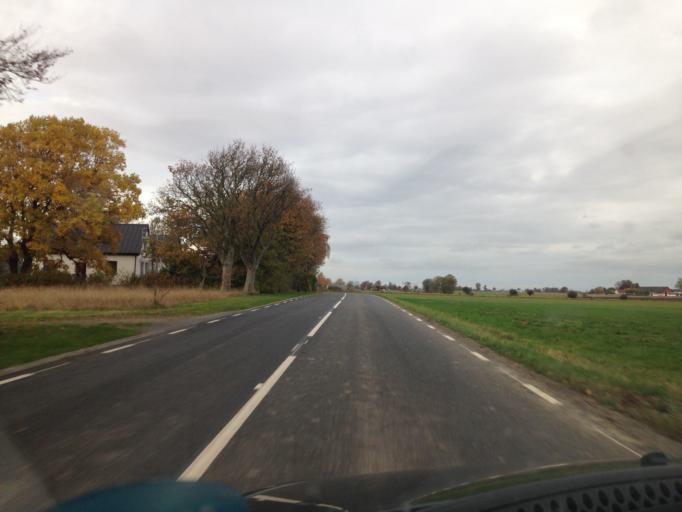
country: SE
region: Skane
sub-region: Simrishamns Kommun
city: Simrishamn
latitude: 55.4317
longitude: 14.1720
